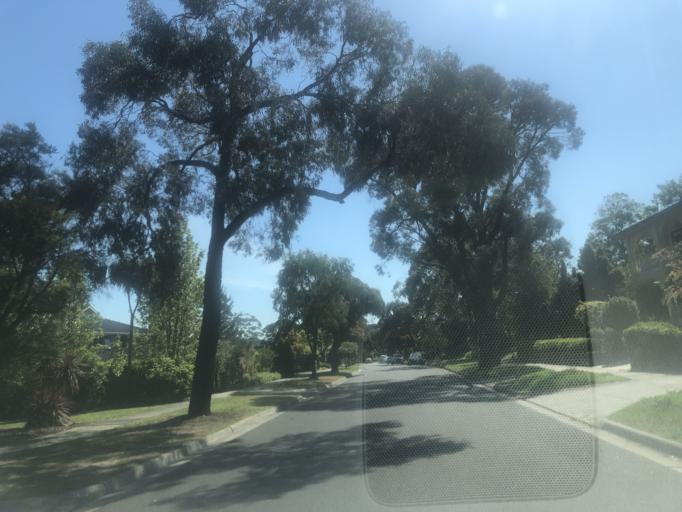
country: AU
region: Victoria
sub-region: Monash
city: Mulgrave
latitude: -37.9037
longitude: 145.1854
